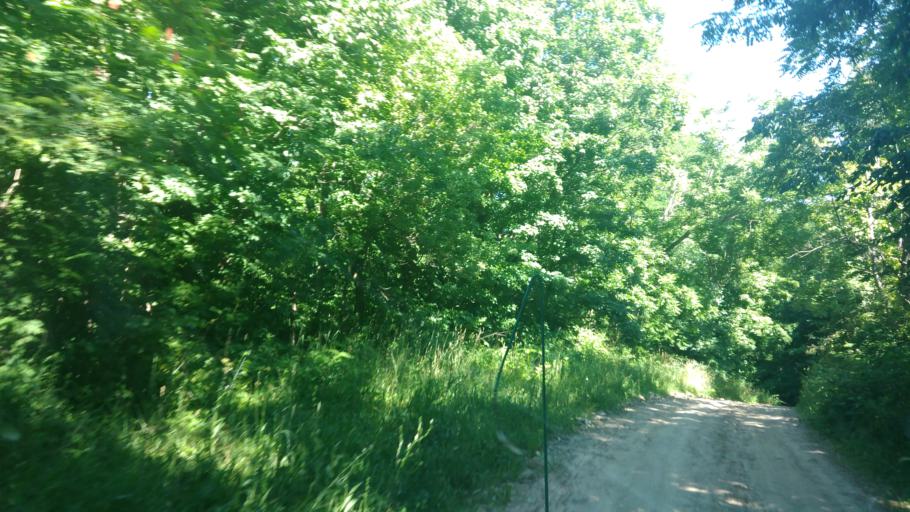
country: US
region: New York
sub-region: Wayne County
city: Clyde
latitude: 43.0251
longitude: -76.8722
